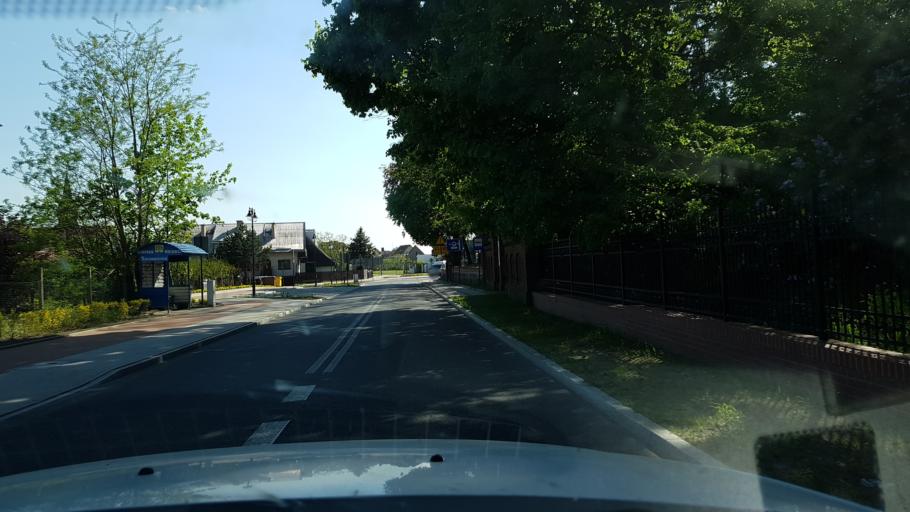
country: PL
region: West Pomeranian Voivodeship
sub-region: Powiat lobeski
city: Resko
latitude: 53.7762
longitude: 15.4079
